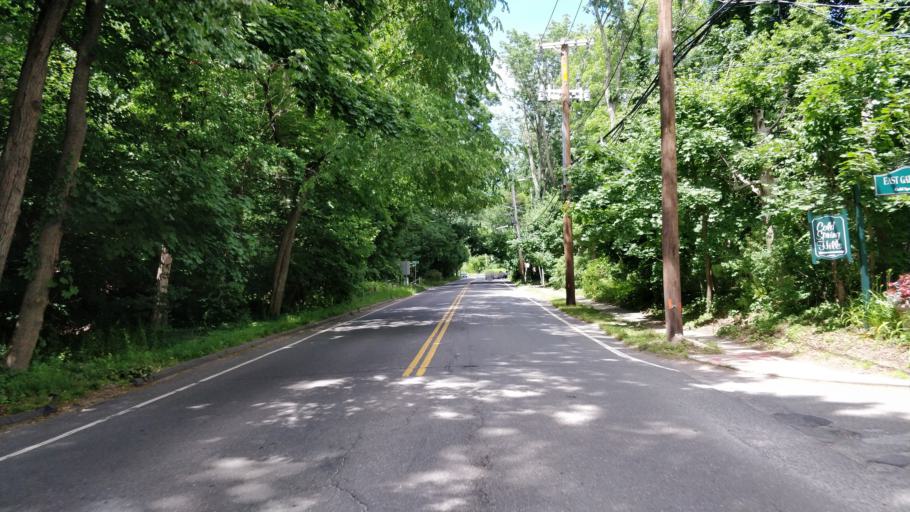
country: US
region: New York
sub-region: Nassau County
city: Woodbury
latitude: 40.8345
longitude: -73.4548
